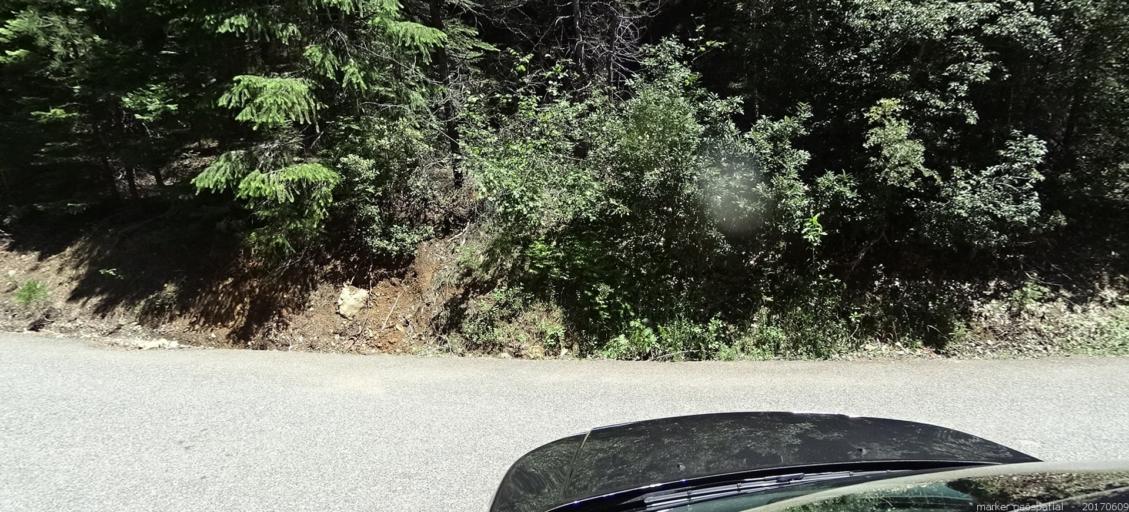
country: US
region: California
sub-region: Siskiyou County
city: Yreka
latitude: 41.3735
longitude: -123.0207
